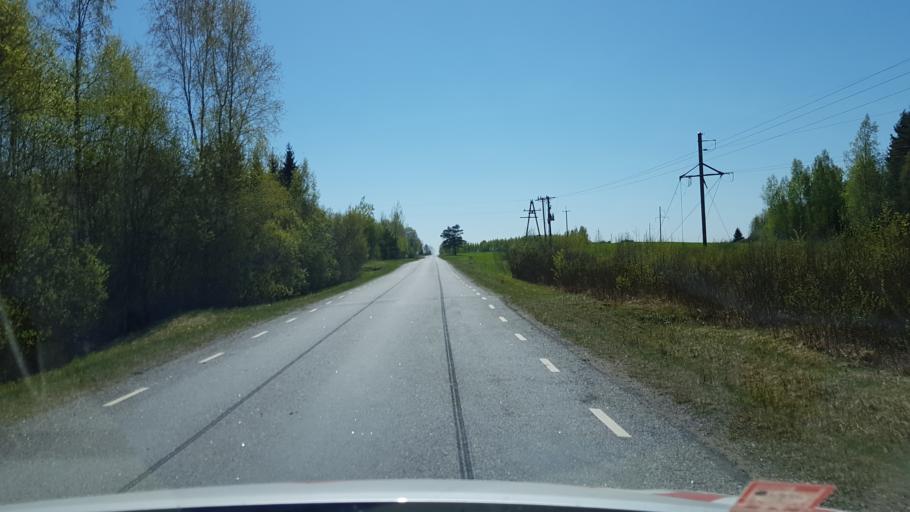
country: EE
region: Vorumaa
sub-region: Voru linn
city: Voru
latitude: 57.9333
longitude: 26.9521
